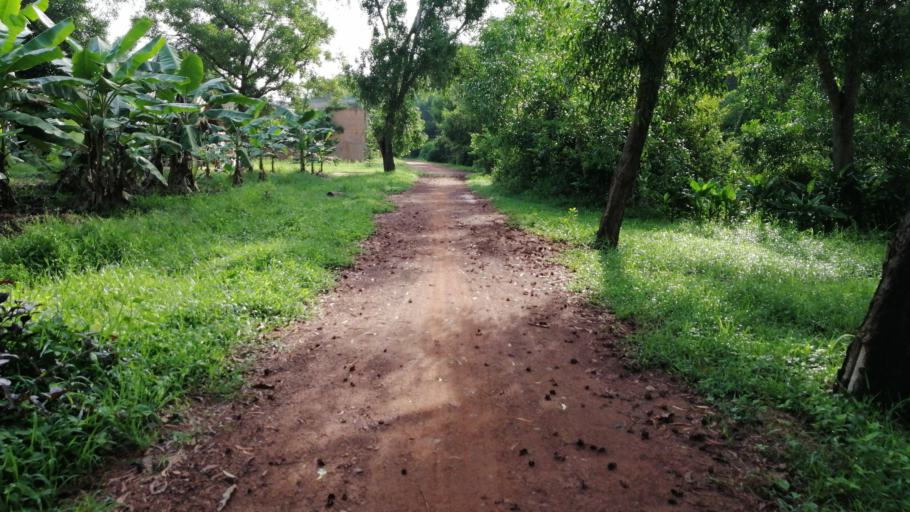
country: KH
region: Siem Reap
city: Siem Reap
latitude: 13.3497
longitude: 103.8187
